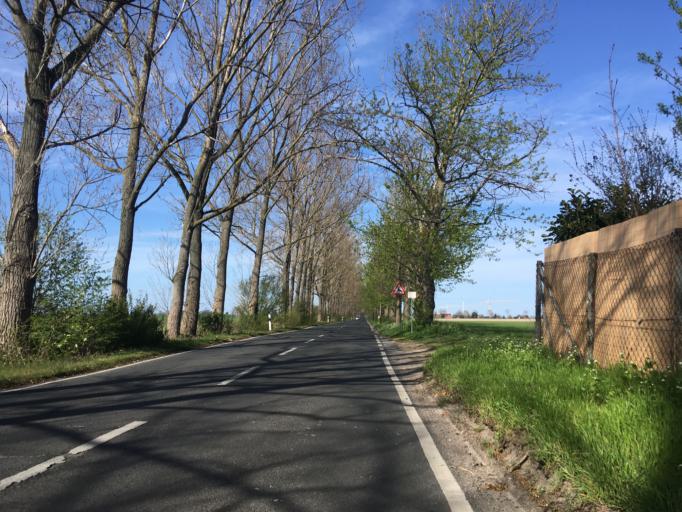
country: DE
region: Berlin
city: Wartenberg
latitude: 52.5850
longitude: 13.5233
